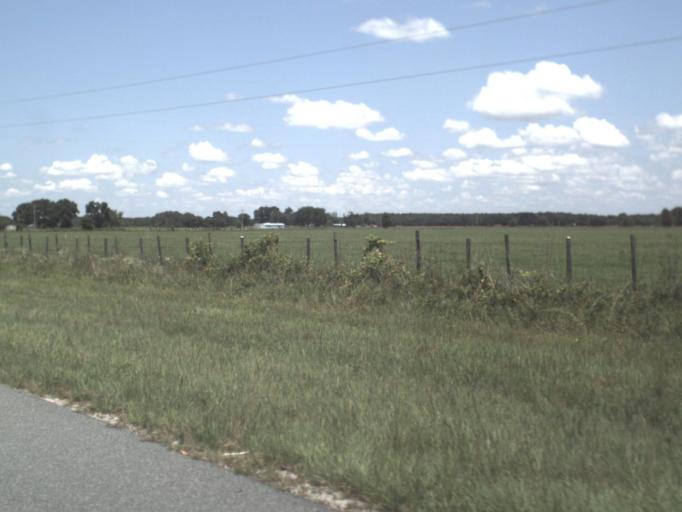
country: US
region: Florida
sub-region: Dixie County
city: Cross City
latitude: 29.8649
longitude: -82.9593
